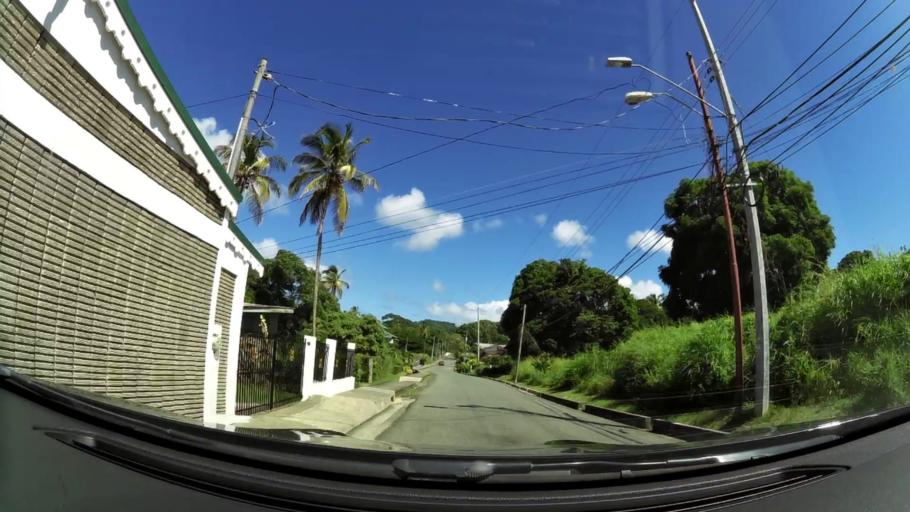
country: TT
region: Tobago
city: Scarborough
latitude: 11.1712
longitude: -60.7822
